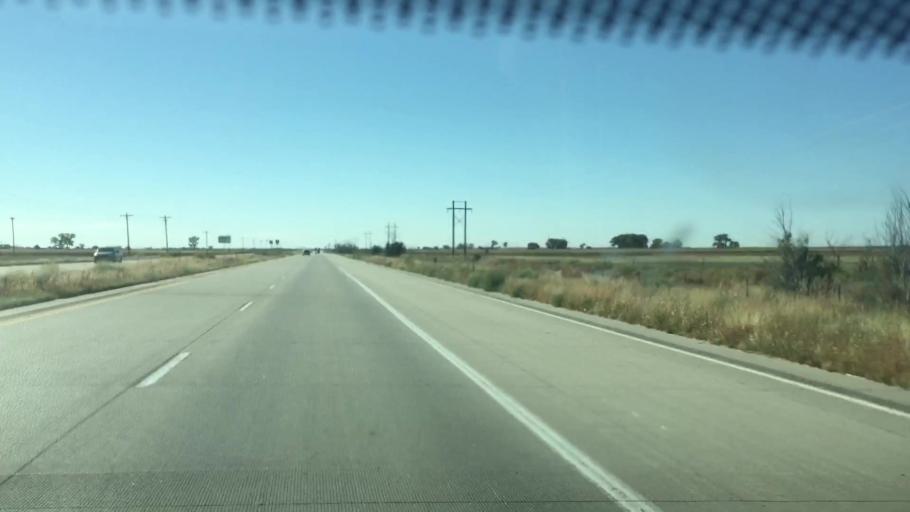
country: US
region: Colorado
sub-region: Prowers County
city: Lamar
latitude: 38.1107
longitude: -102.6706
